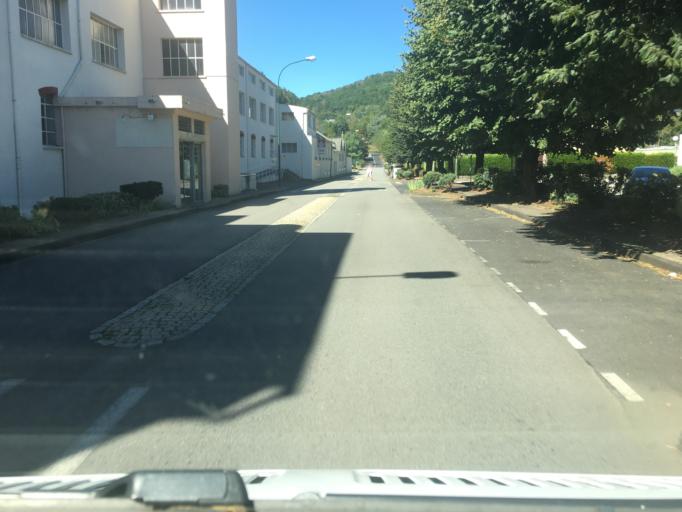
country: FR
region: Limousin
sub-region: Departement de la Correze
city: Bort-les-Orgues
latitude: 45.4087
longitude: 2.5027
